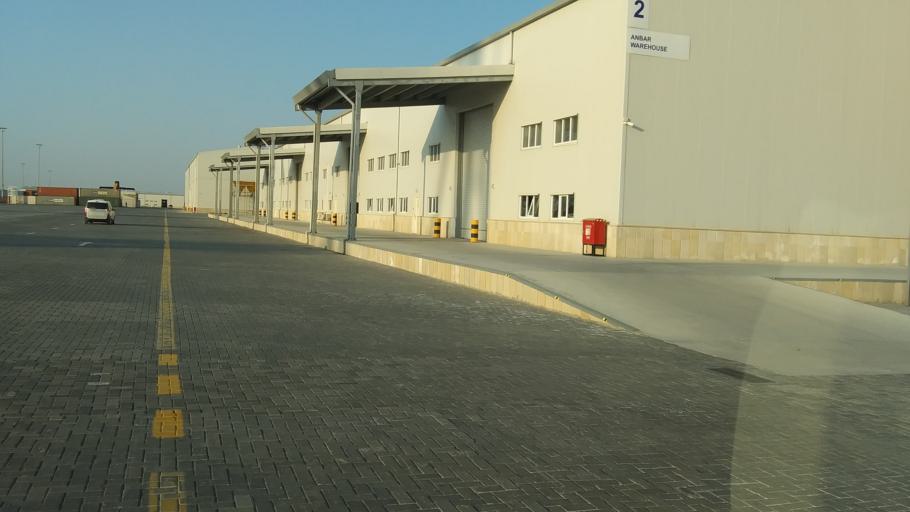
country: AZ
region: Baki
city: Qobustan
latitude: 39.9730
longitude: 49.4499
